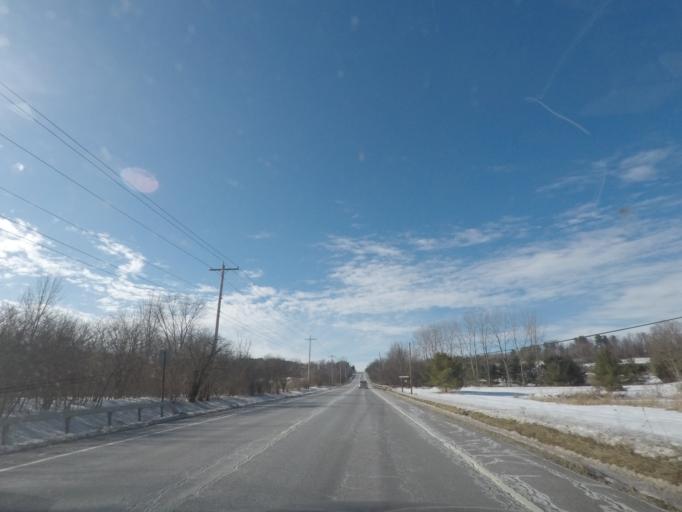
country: US
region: New York
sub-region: Albany County
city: Altamont
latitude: 42.7455
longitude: -74.0330
